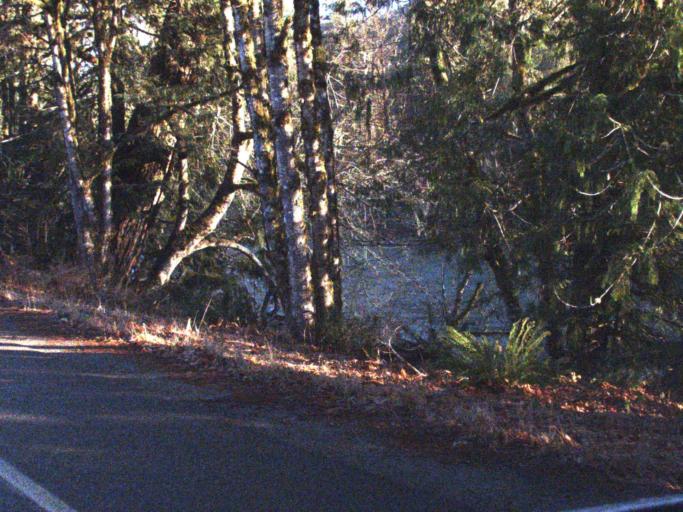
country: US
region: Washington
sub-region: Snohomish County
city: Darrington
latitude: 48.5478
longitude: -121.4245
